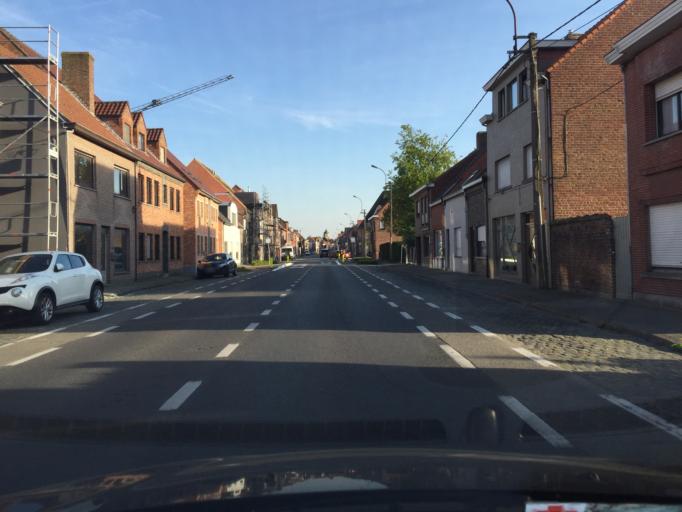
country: BE
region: Flanders
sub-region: Provincie Oost-Vlaanderen
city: Maldegem
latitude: 51.2179
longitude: 3.4471
